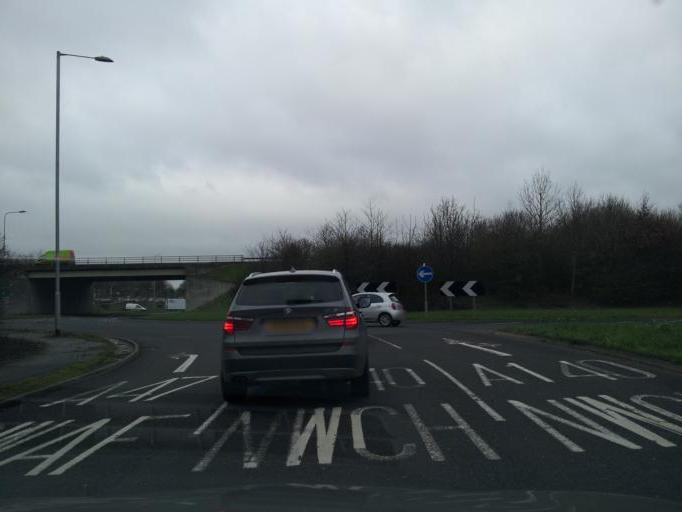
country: GB
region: England
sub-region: Norfolk
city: Cringleford
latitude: 52.5873
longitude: 1.2755
